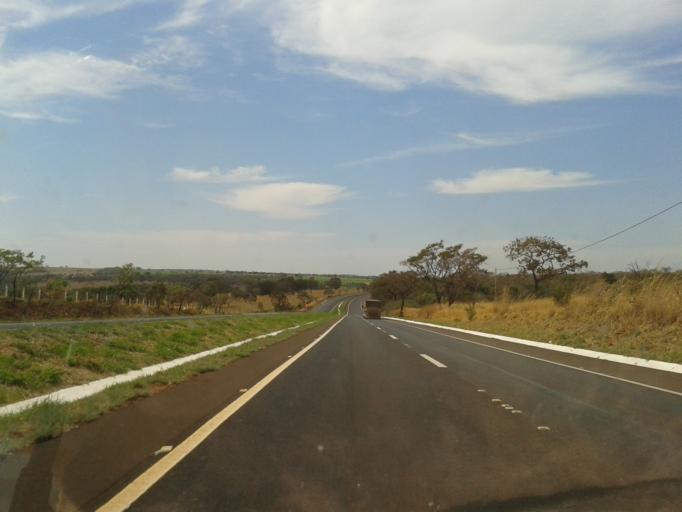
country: BR
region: Minas Gerais
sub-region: Monte Alegre De Minas
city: Monte Alegre de Minas
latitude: -18.8923
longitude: -48.6791
